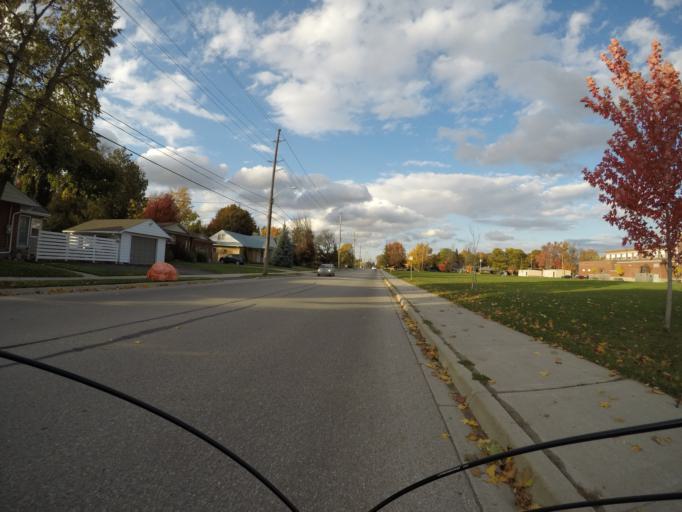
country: CA
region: Ontario
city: Waterloo
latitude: 43.5935
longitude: -80.5641
